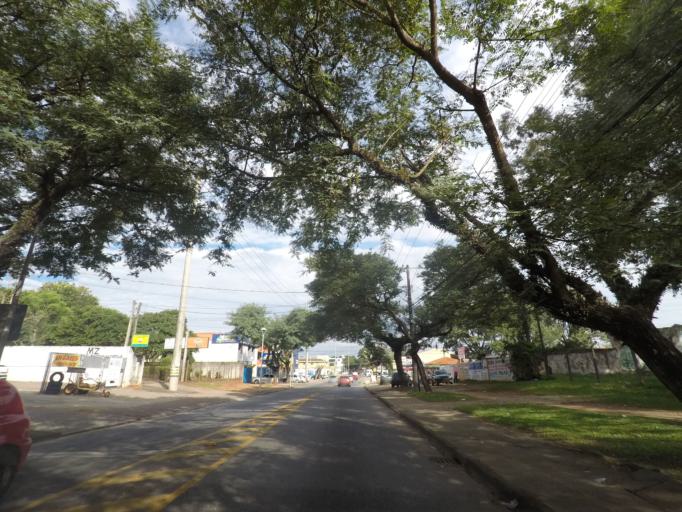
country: BR
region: Parana
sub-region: Sao Jose Dos Pinhais
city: Sao Jose dos Pinhais
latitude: -25.5381
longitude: -49.2948
